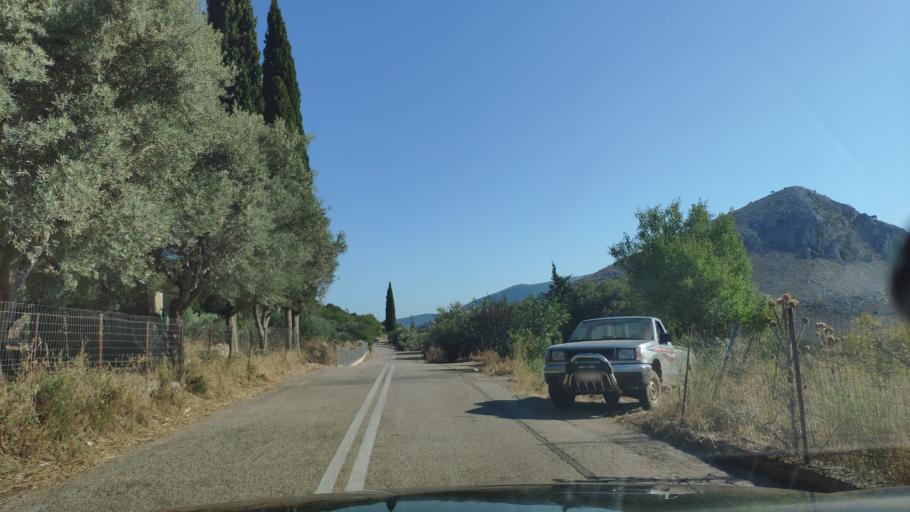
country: GR
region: West Greece
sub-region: Nomos Aitolias kai Akarnanias
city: Archontochorion
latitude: 38.6982
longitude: 21.0407
